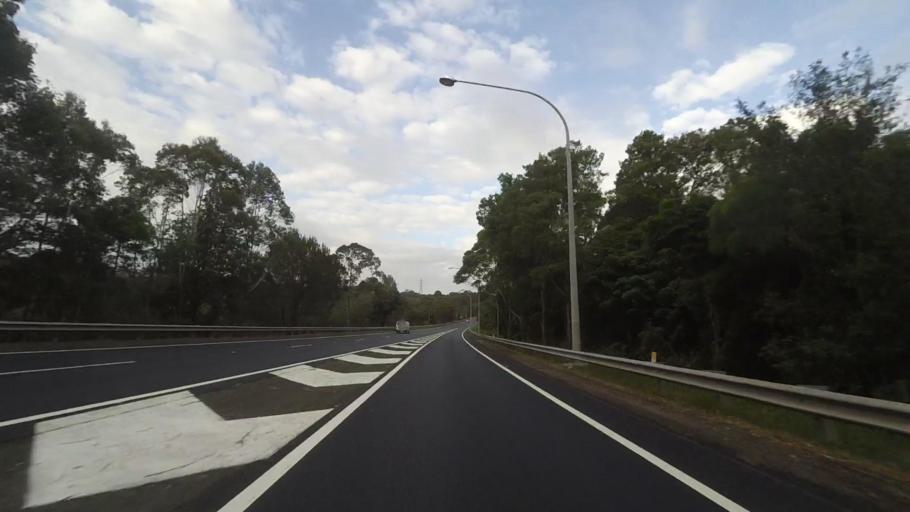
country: AU
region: New South Wales
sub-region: Wollongong
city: Bulli
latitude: -34.3075
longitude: 150.8995
